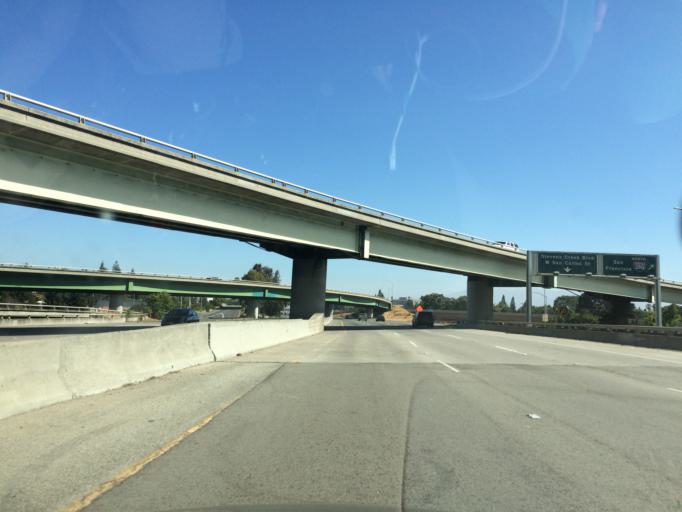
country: US
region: California
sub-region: Santa Clara County
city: Burbank
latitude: 37.3167
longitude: -121.9403
